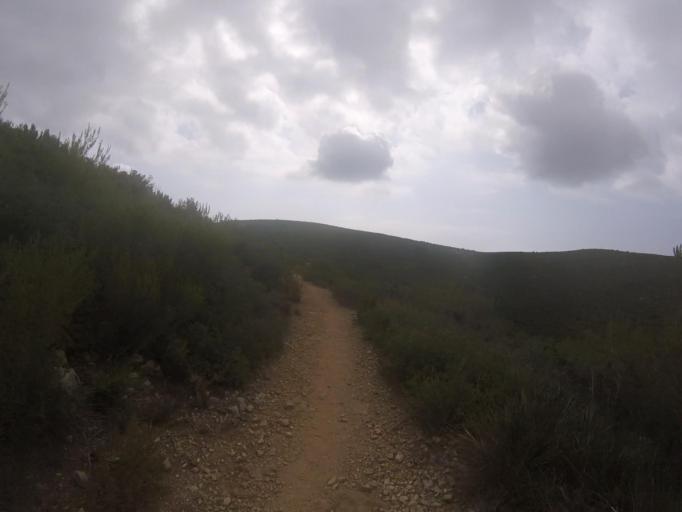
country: ES
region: Valencia
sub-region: Provincia de Castello
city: Santa Magdalena de Pulpis
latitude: 40.3472
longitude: 0.3471
